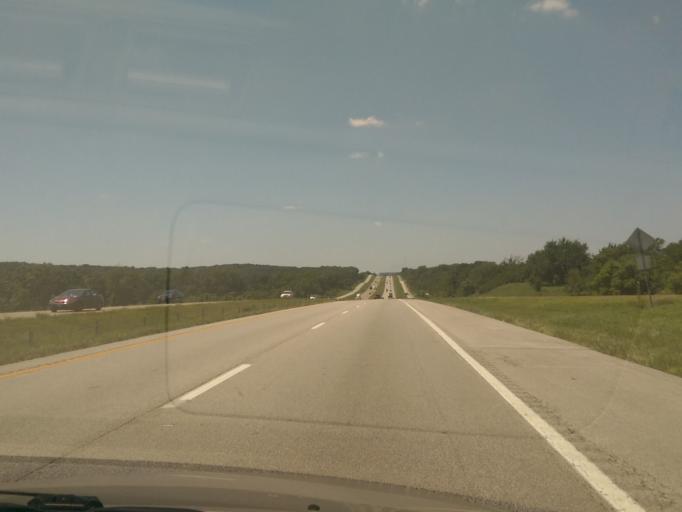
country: US
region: Missouri
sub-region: Cooper County
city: Boonville
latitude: 38.9353
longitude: -92.8683
